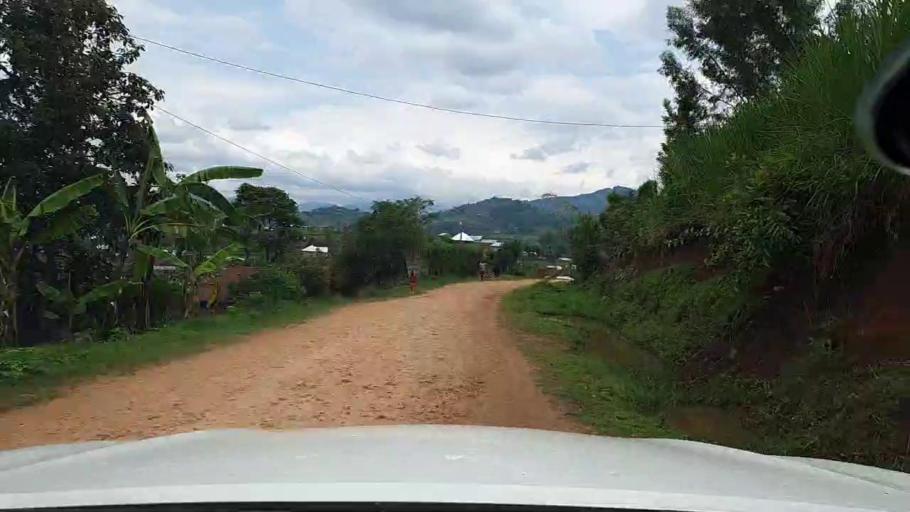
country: RW
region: Western Province
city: Kibuye
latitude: -2.0731
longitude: 29.4240
